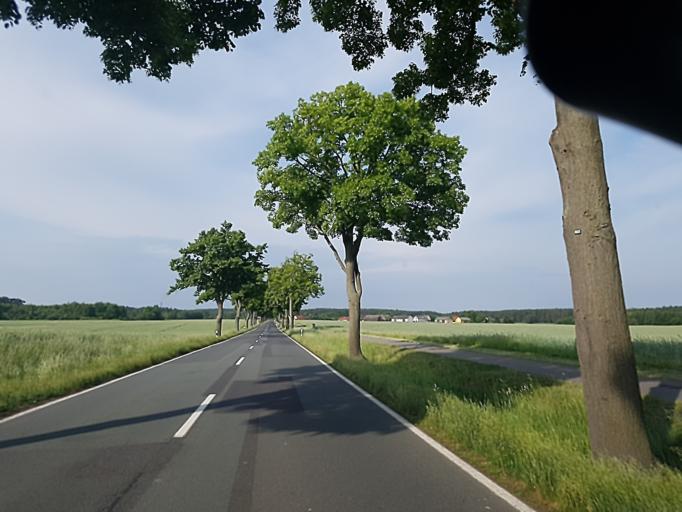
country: DE
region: Brandenburg
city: Niemegk
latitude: 52.0588
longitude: 12.6721
